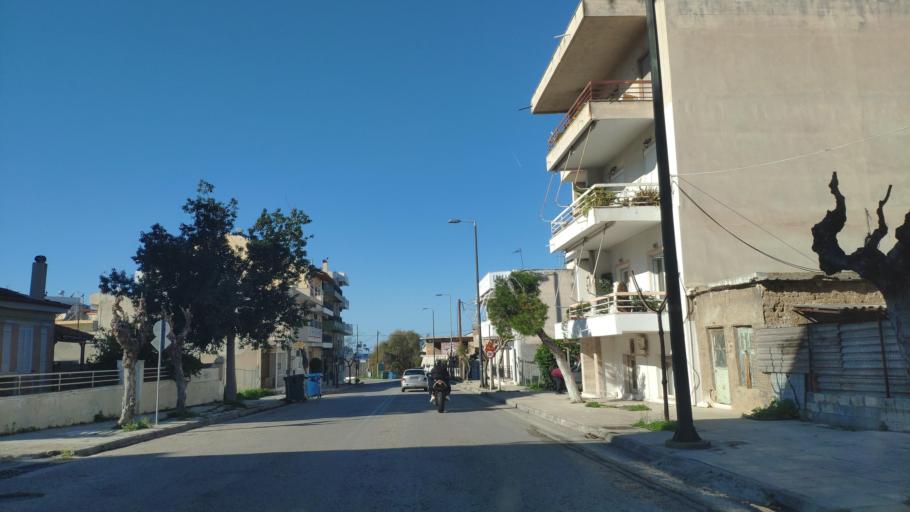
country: GR
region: Peloponnese
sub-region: Nomos Korinthias
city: Korinthos
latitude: 37.9406
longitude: 22.9475
